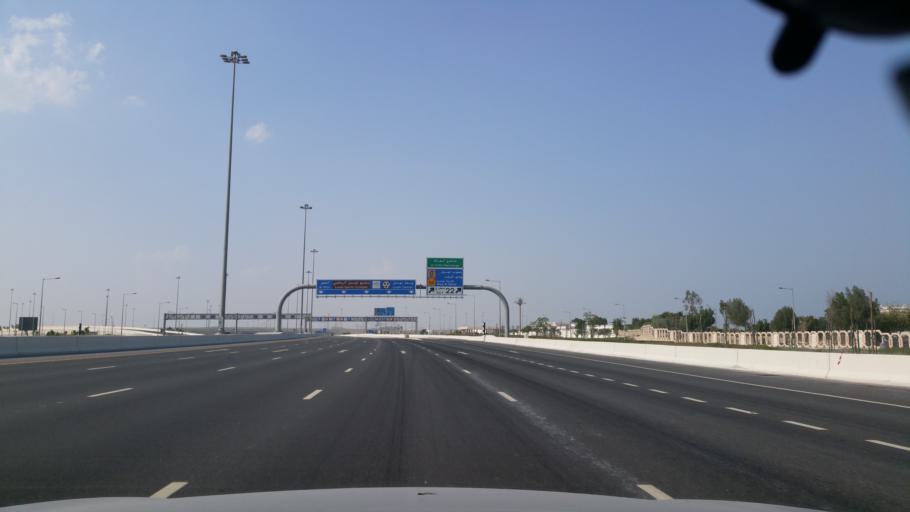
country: QA
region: Baladiyat Umm Salal
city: Umm Salal Muhammad
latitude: 25.3865
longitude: 51.5000
